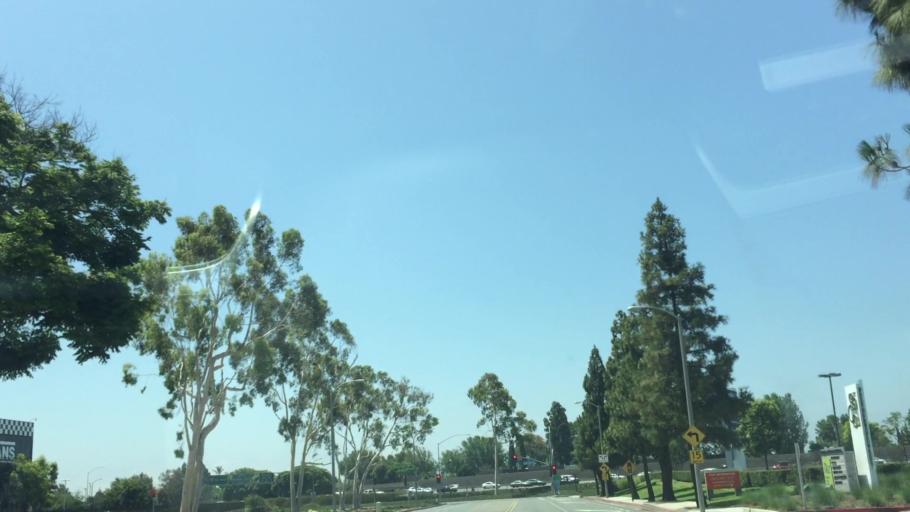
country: US
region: California
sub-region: Orange County
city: Fountain Valley
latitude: 33.6934
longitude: -117.9249
